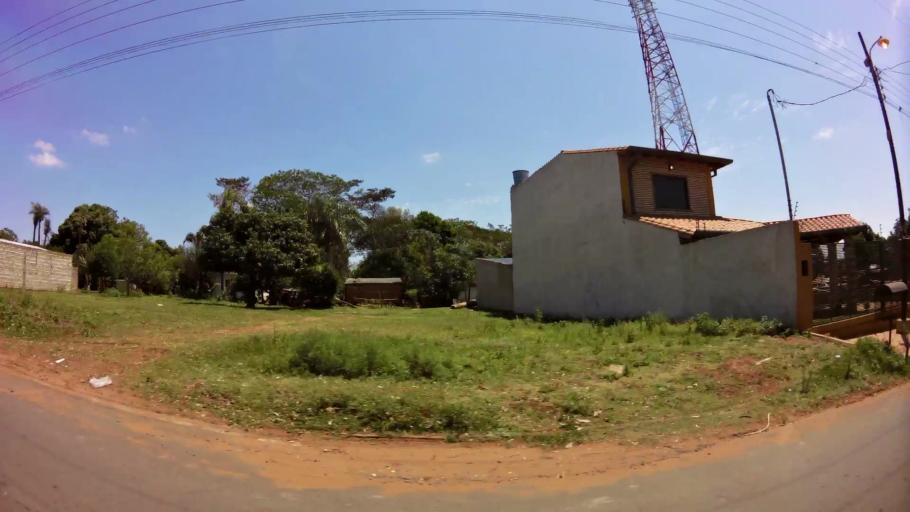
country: PY
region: Central
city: San Antonio
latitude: -25.4151
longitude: -57.5259
